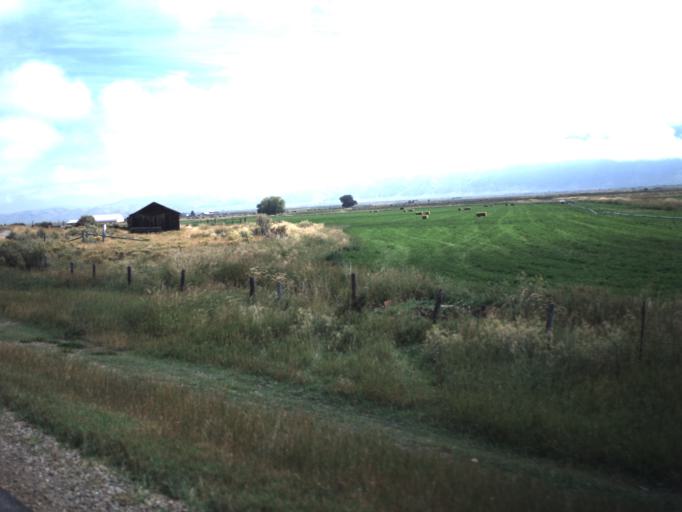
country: US
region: Utah
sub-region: Rich County
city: Randolph
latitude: 41.6790
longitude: -111.1832
